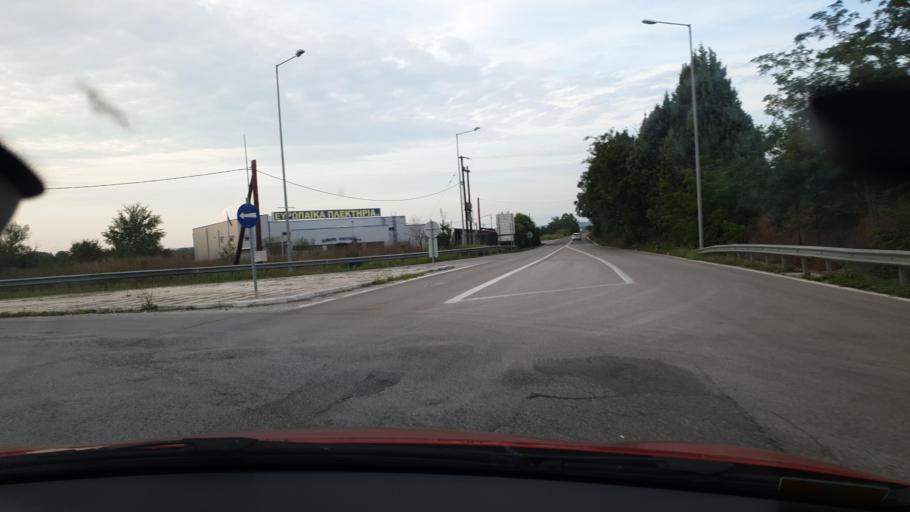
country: GR
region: Central Macedonia
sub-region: Nomos Kilkis
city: Nea Santa
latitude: 40.8469
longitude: 22.9053
